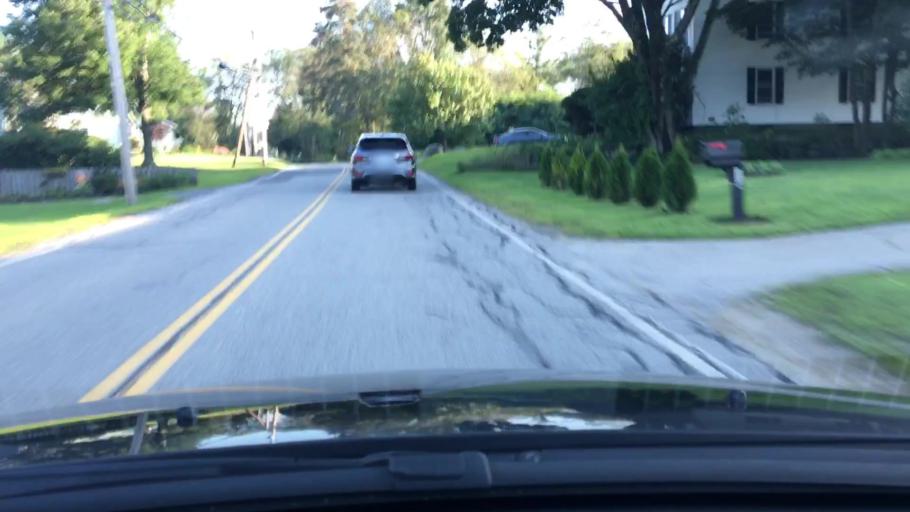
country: US
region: Massachusetts
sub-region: Worcester County
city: West Boylston
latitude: 42.3516
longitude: -71.7791
